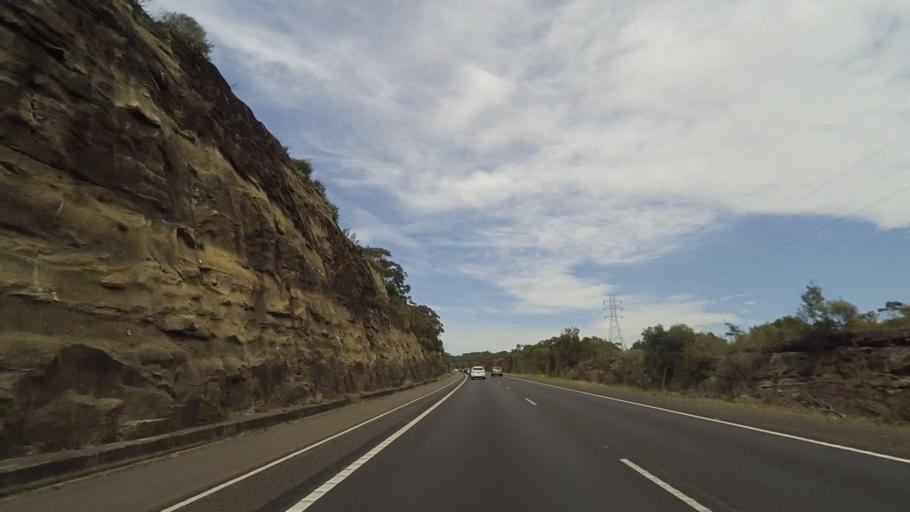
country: AU
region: New South Wales
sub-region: Wollongong
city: Helensburgh
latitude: -34.1920
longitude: 150.9670
